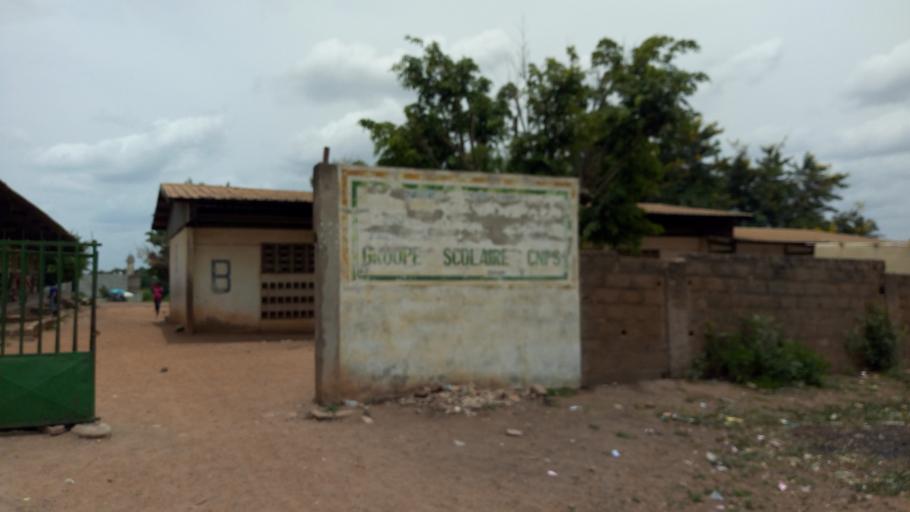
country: CI
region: Vallee du Bandama
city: Bouake
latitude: 7.7075
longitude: -5.0346
